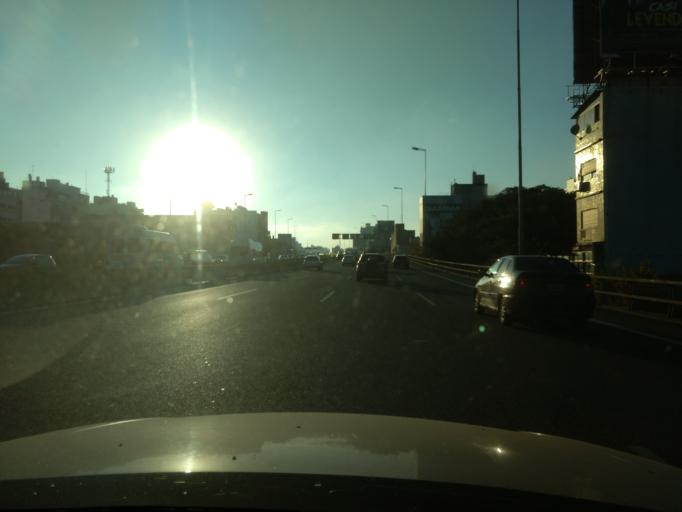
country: AR
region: Buenos Aires F.D.
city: Buenos Aires
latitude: -34.6263
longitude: -58.4039
